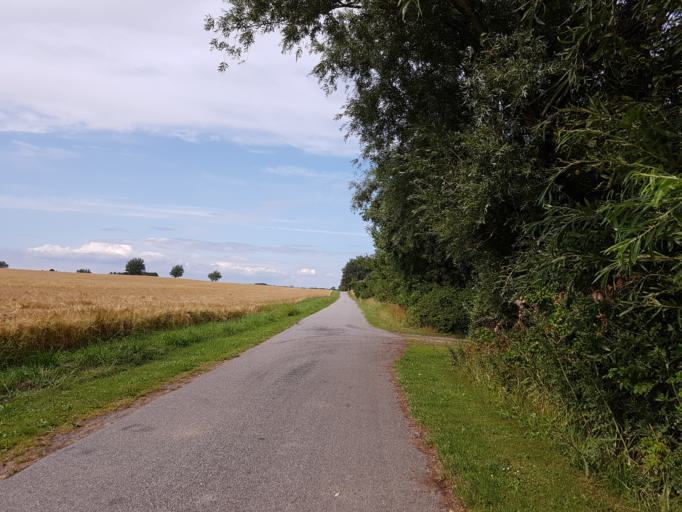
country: DK
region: Zealand
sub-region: Guldborgsund Kommune
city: Nykobing Falster
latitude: 54.5690
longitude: 11.9676
